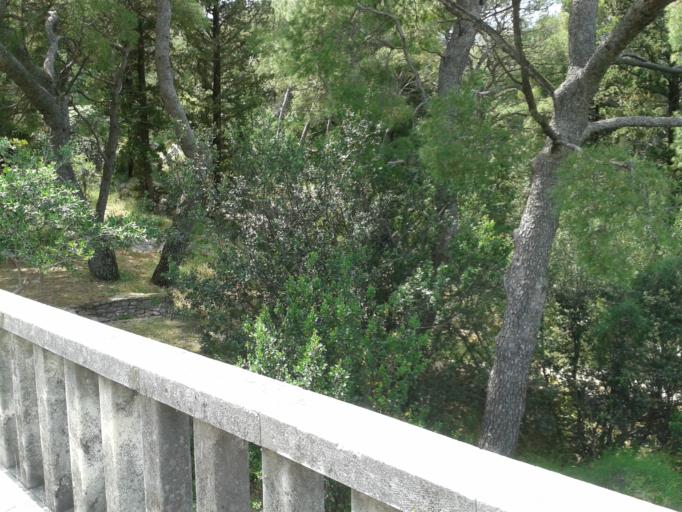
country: HR
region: Splitsko-Dalmatinska
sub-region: Grad Split
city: Split
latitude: 43.5106
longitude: 16.4214
